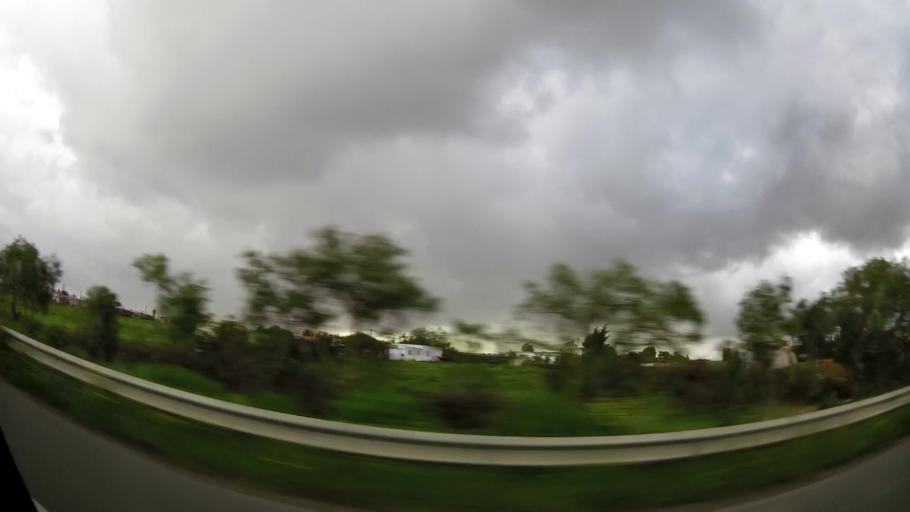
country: MA
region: Grand Casablanca
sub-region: Mediouna
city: Tit Mellil
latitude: 33.5714
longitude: -7.4587
